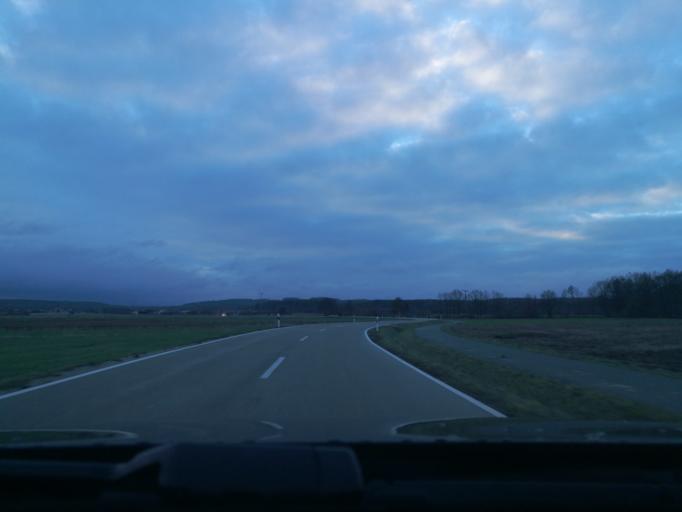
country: DE
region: Bavaria
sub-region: Regierungsbezirk Mittelfranken
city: Baiersdorf
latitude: 49.6480
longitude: 11.0473
